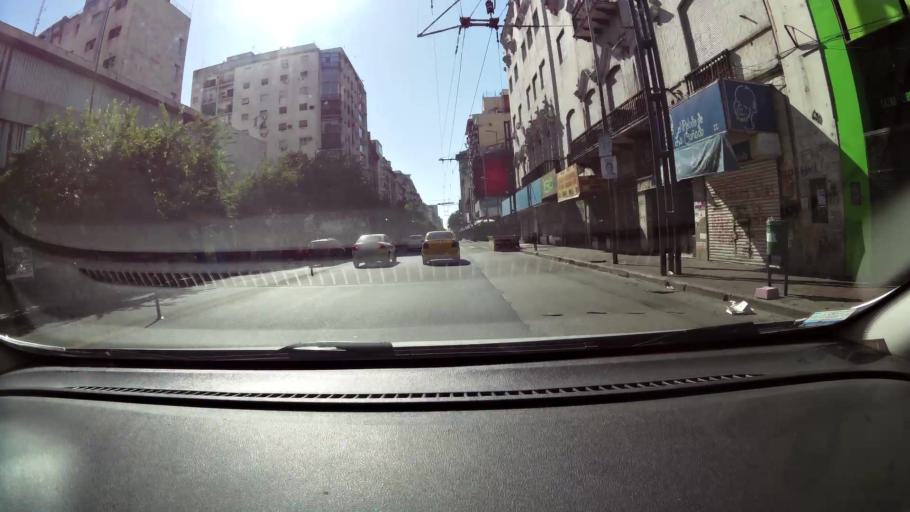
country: AR
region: Cordoba
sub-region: Departamento de Capital
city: Cordoba
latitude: -31.4125
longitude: -64.1862
